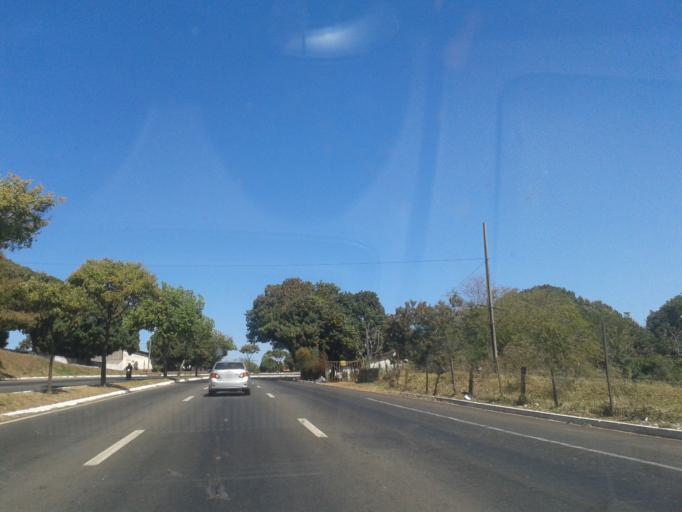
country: BR
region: Goias
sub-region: Goiania
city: Goiania
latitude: -16.6418
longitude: -49.2861
